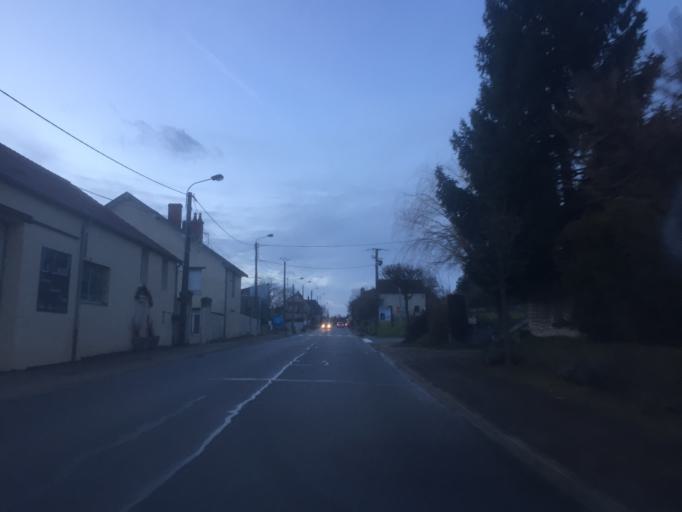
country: FR
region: Franche-Comte
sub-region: Departement du Jura
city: Orchamps
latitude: 47.1458
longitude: 5.6655
